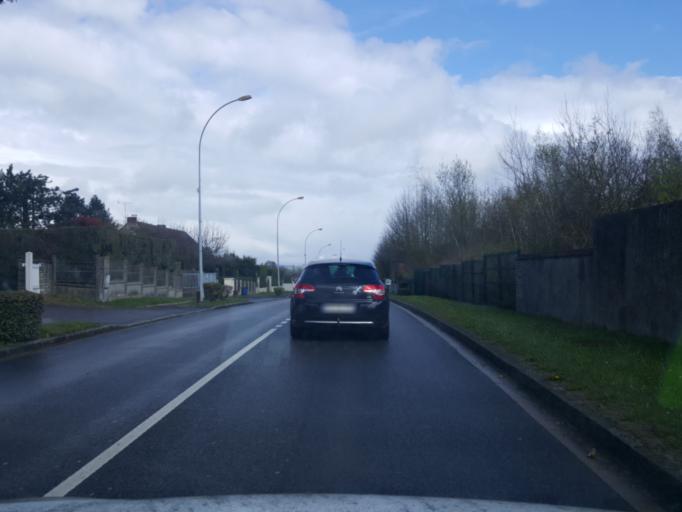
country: FR
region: Picardie
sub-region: Departement de l'Oise
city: Auneuil
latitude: 49.3735
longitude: 1.9897
